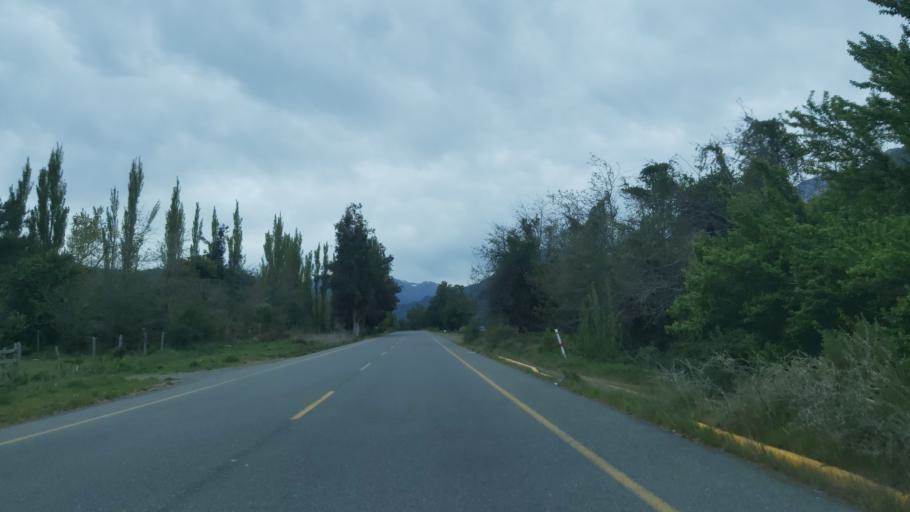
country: CL
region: Maule
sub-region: Provincia de Linares
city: Colbun
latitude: -35.7460
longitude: -71.0072
